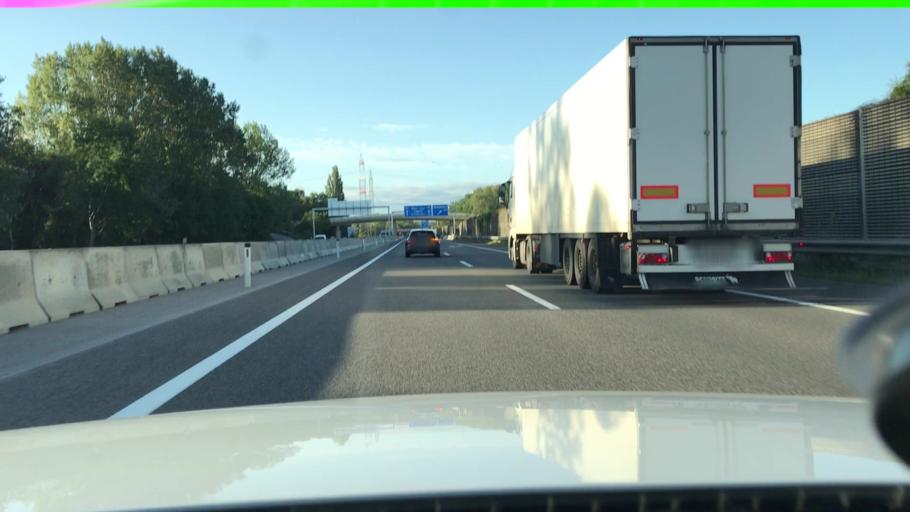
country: AT
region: Lower Austria
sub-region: Politischer Bezirk Sankt Polten
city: Herzogenburg
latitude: 48.2709
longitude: 15.6996
